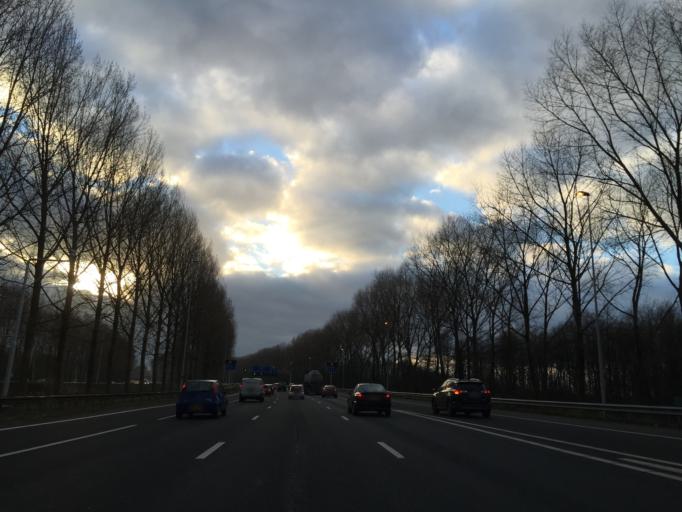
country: NL
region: South Holland
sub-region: Bodegraven-Reeuwijk
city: Bodegraven
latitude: 52.0647
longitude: 4.7386
